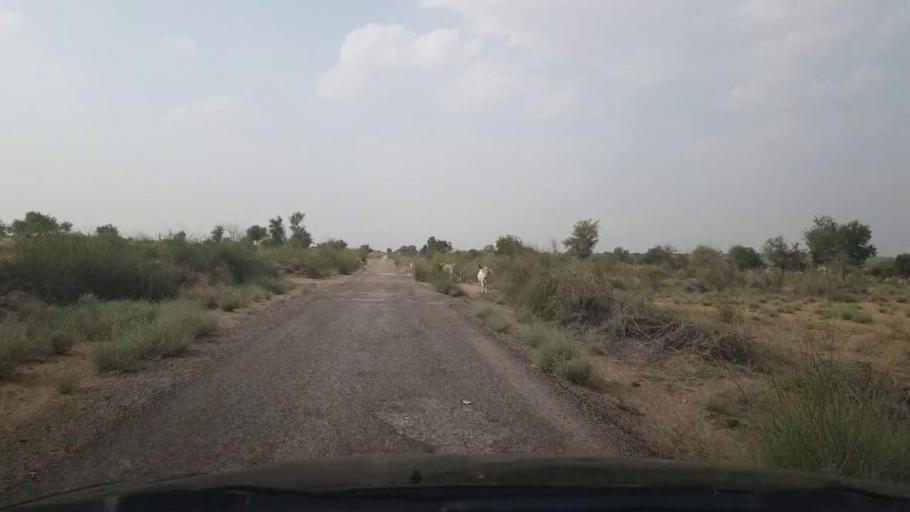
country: PK
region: Sindh
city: Islamkot
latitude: 24.9748
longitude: 70.5866
